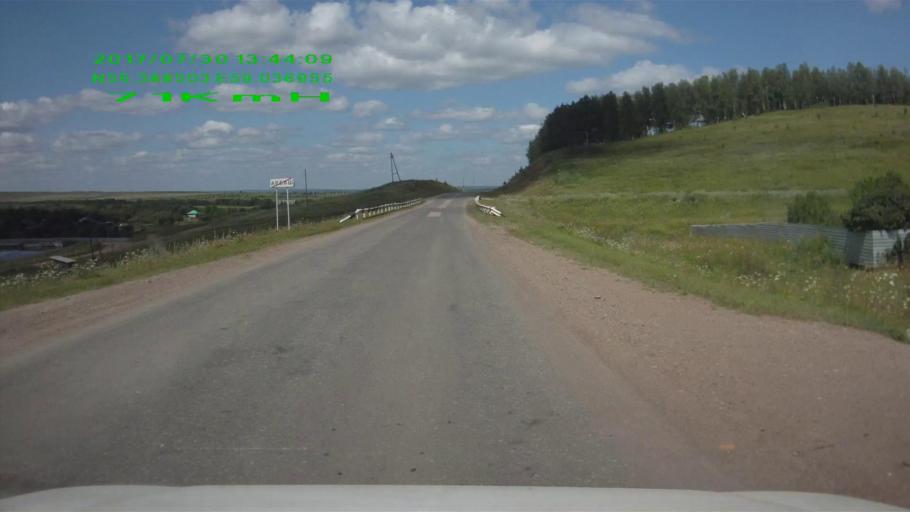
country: RU
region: Sverdlovsk
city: Mikhaylovsk
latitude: 56.3887
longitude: 59.0369
